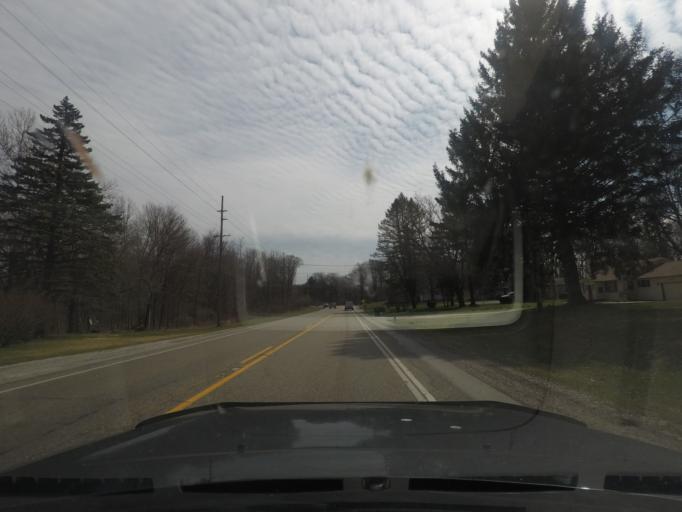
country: US
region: Indiana
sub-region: LaPorte County
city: LaPorte
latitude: 41.6533
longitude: -86.7622
